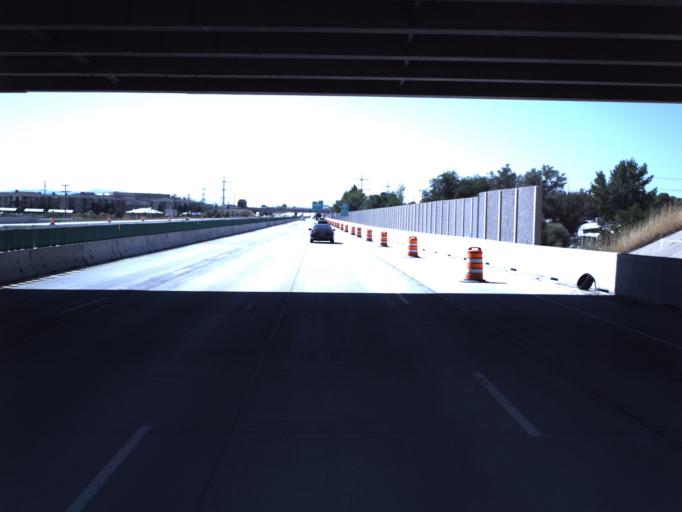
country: US
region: Utah
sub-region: Salt Lake County
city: Taylorsville
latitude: 40.7124
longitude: -111.9540
